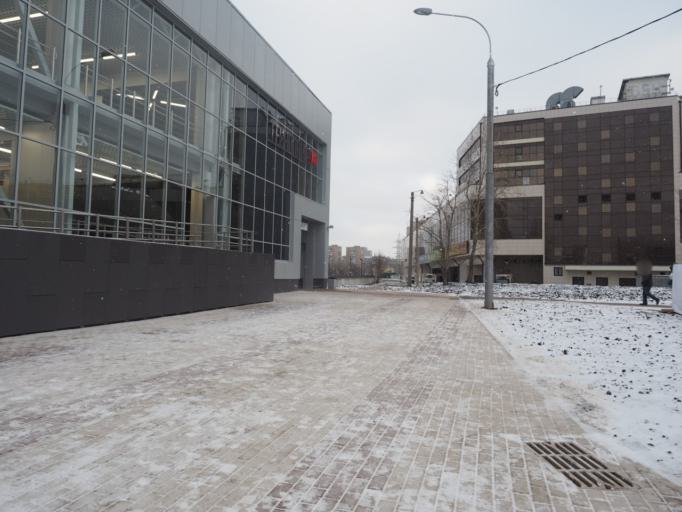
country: RU
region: Moskovskaya
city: Kozhukhovo
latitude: 55.6946
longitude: 37.6647
